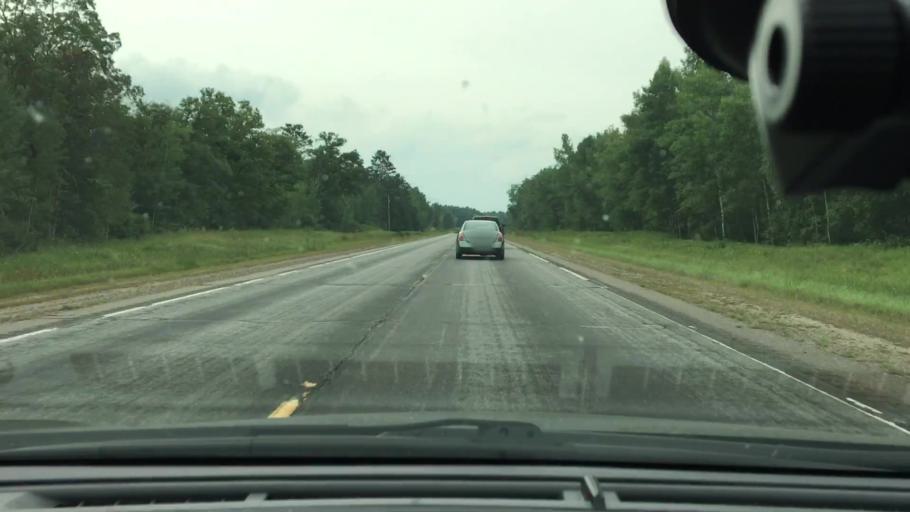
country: US
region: Minnesota
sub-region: Crow Wing County
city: Cross Lake
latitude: 46.6768
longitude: -93.9525
